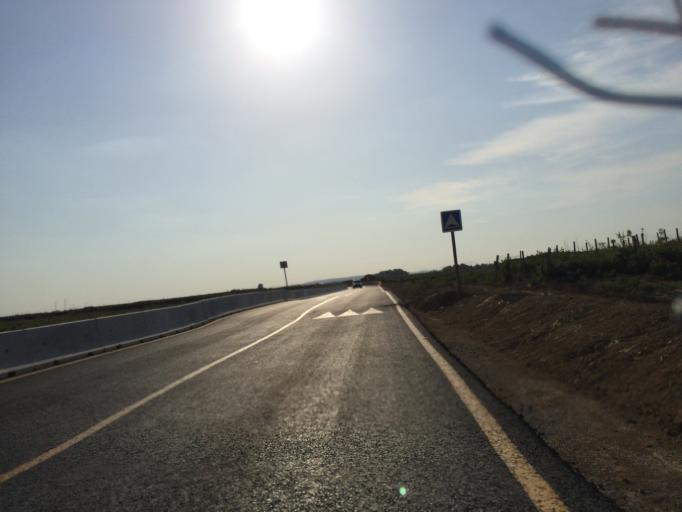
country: FR
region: Ile-de-France
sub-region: Departement de l'Essonne
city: Bondoufle
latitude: 48.6156
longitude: 2.3635
